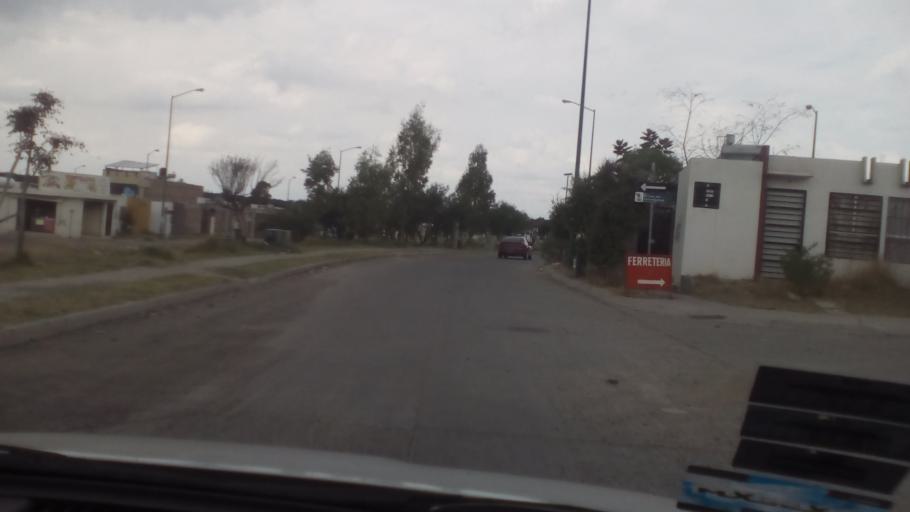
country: MX
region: Guanajuato
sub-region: Leon
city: Fraccionamiento Paseo de las Torres
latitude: 21.1896
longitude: -101.7649
